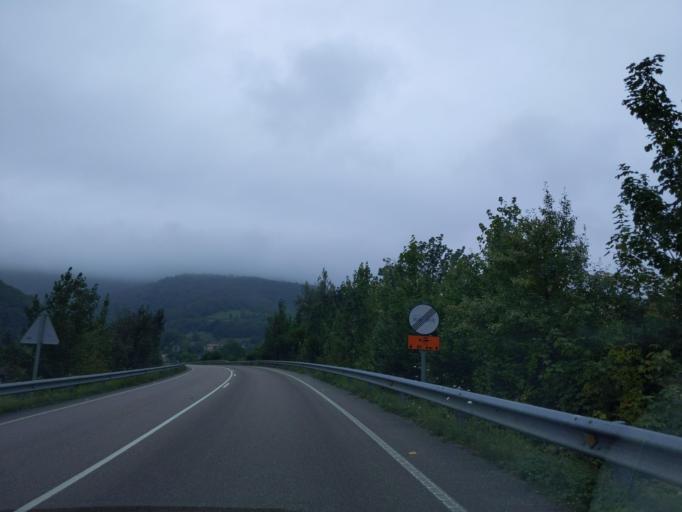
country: ES
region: Asturias
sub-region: Province of Asturias
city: Pola de Laviana
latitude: 43.2351
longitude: -5.5256
